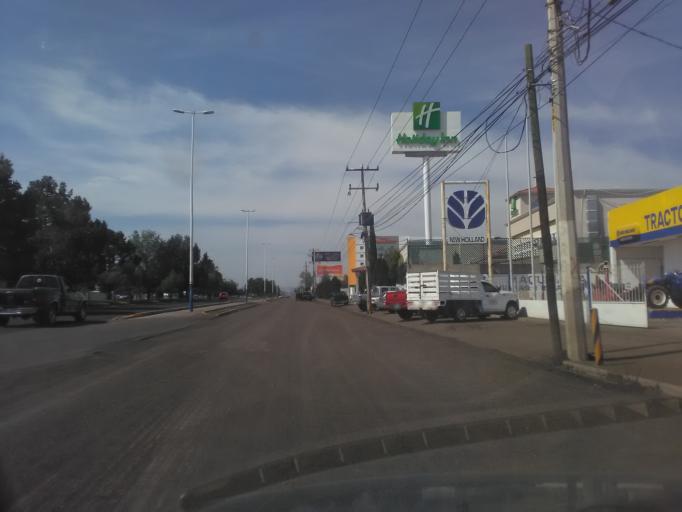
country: MX
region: Durango
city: Victoria de Durango
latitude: 24.0562
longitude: -104.6138
